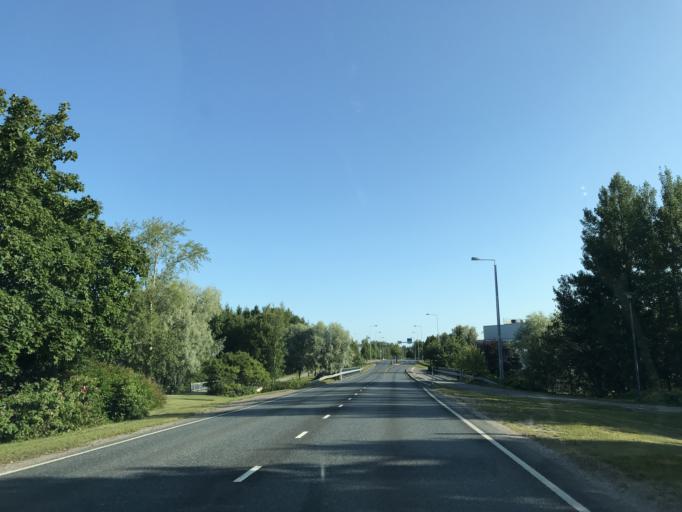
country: FI
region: Paijanne Tavastia
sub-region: Lahti
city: Orimattila
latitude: 60.8034
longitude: 25.7287
